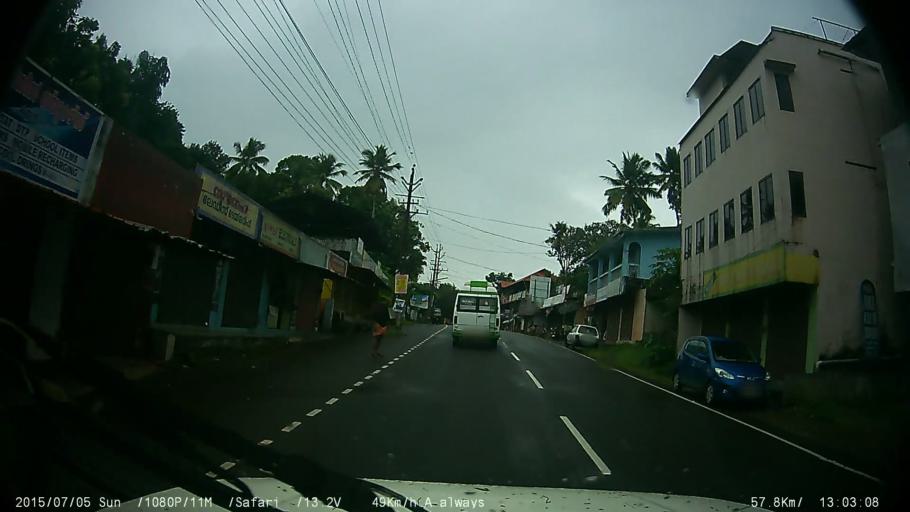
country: IN
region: Kerala
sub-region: Kottayam
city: Changanacheri
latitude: 9.4958
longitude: 76.5731
